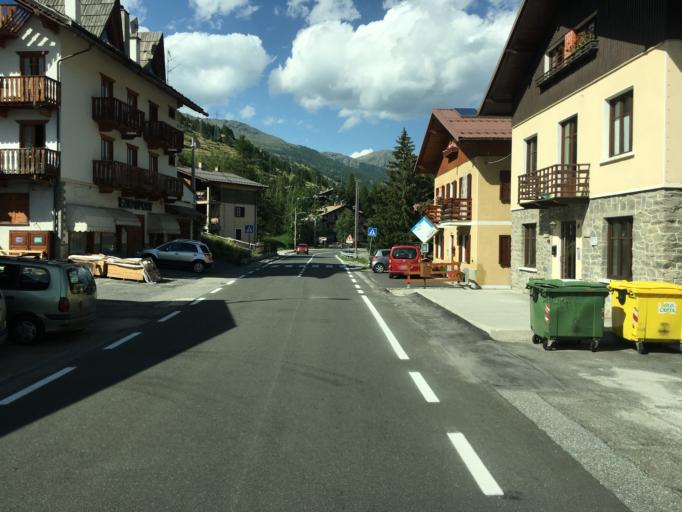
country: IT
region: Piedmont
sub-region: Provincia di Torino
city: Pragelato-Rua
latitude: 45.0092
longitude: 6.9346
